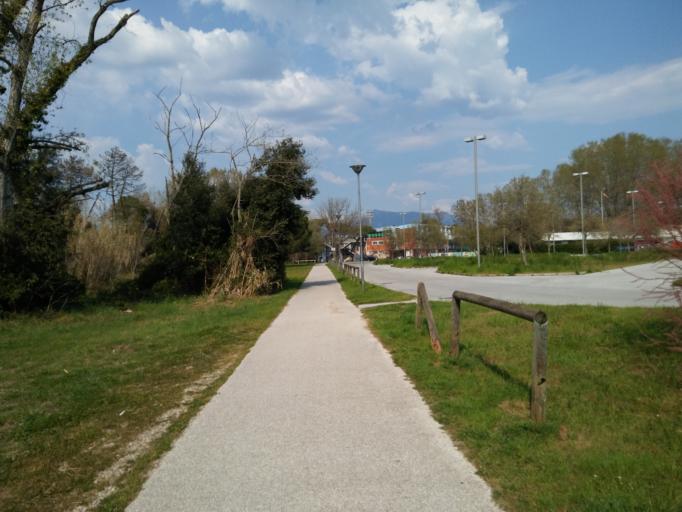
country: IT
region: Tuscany
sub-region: Provincia di Lucca
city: Viareggio
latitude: 43.8569
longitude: 10.2465
